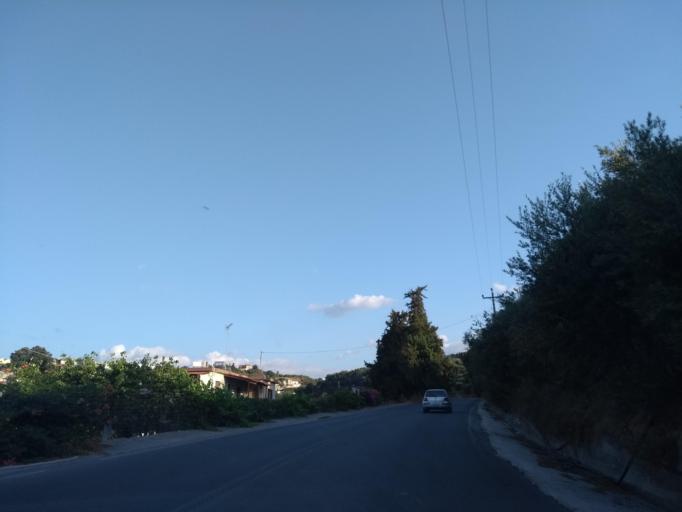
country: GR
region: Crete
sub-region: Nomos Chanias
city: Kalivai
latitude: 35.4380
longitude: 24.1757
